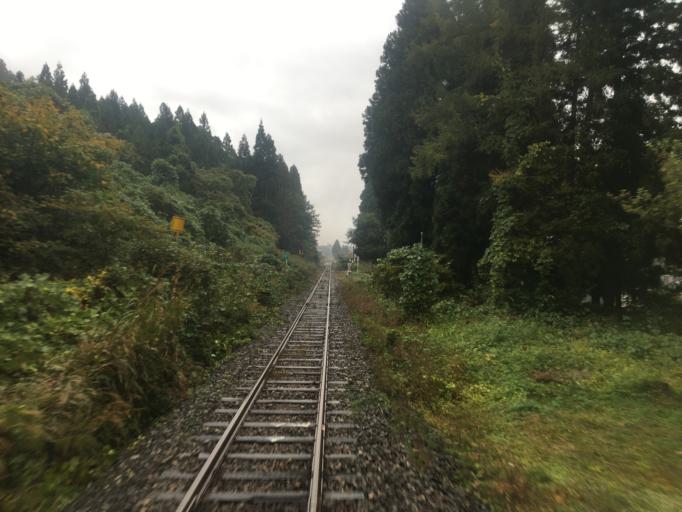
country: JP
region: Yamagata
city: Shinjo
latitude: 38.7650
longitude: 140.4468
